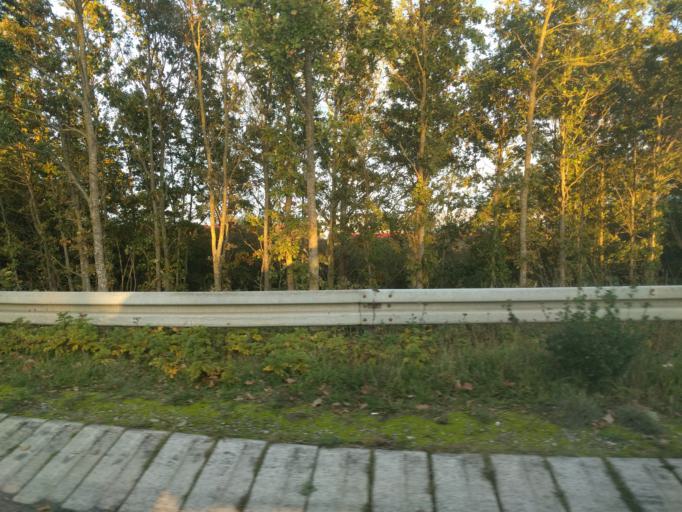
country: DK
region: South Denmark
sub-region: Kerteminde Kommune
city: Langeskov
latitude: 55.3558
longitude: 10.6100
